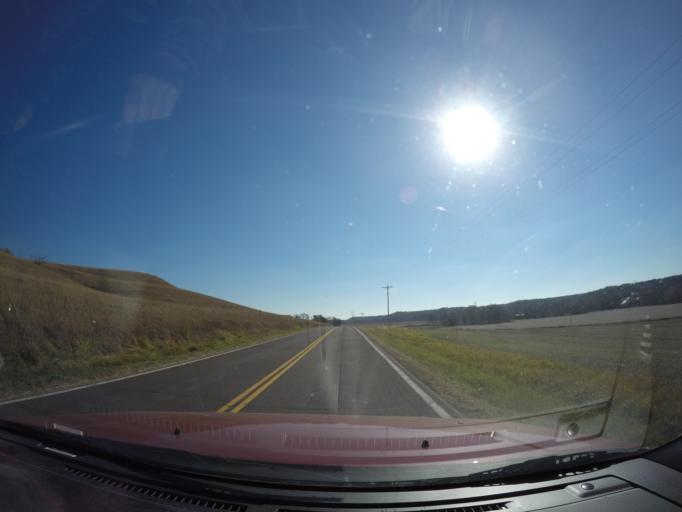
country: US
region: Kansas
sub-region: Geary County
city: Grandview Plaza
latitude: 38.9876
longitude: -96.7254
